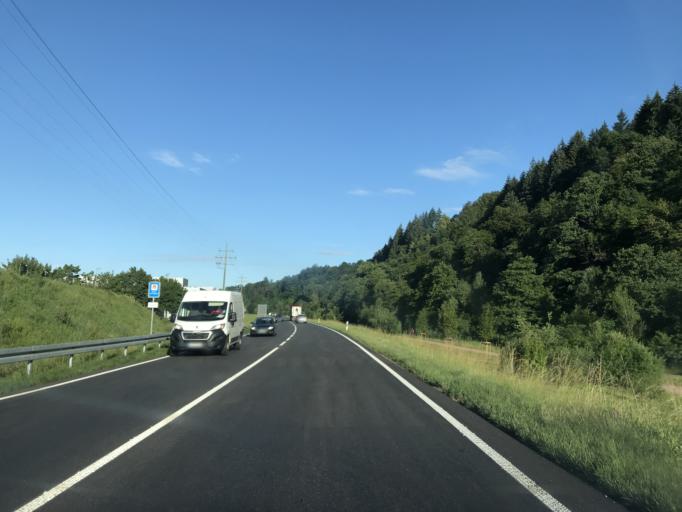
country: DE
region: Baden-Wuerttemberg
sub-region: Freiburg Region
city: Maulburg
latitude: 47.6491
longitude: 7.7860
